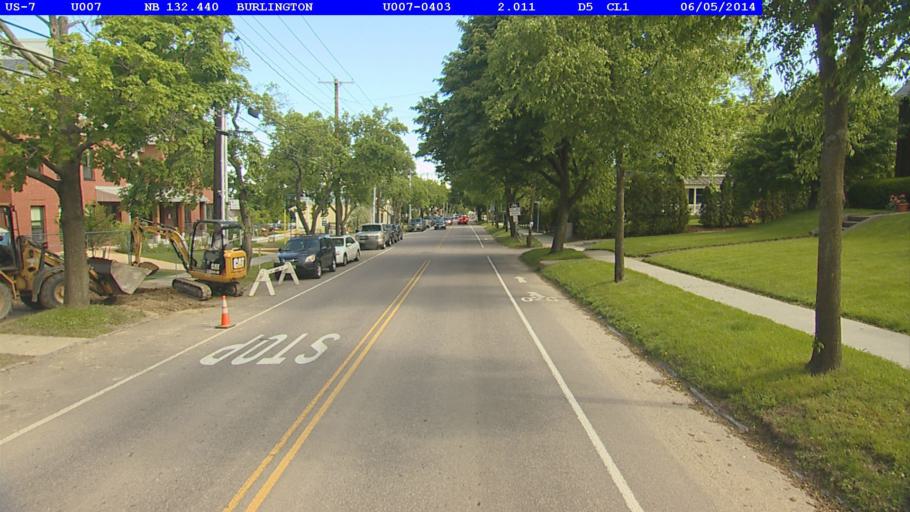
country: US
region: Vermont
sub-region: Chittenden County
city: Burlington
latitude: 44.4746
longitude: -73.2053
